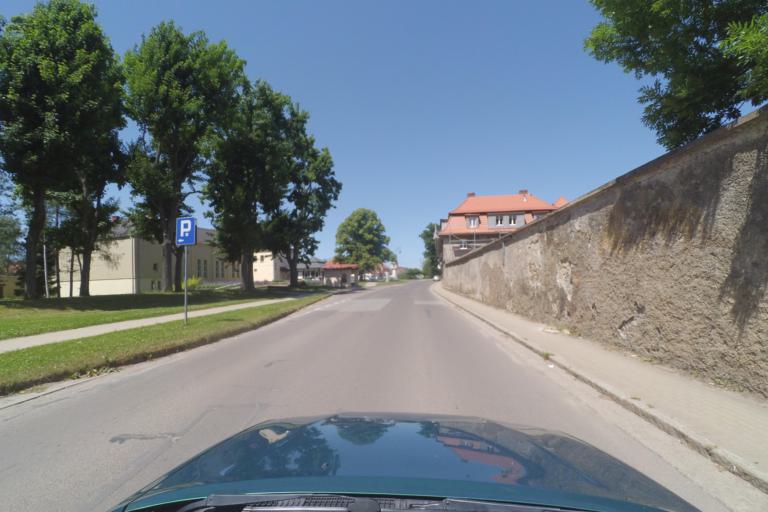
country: PL
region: Lower Silesian Voivodeship
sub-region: Powiat kamiennogorski
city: Krzeszow
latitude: 50.7316
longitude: 16.0674
